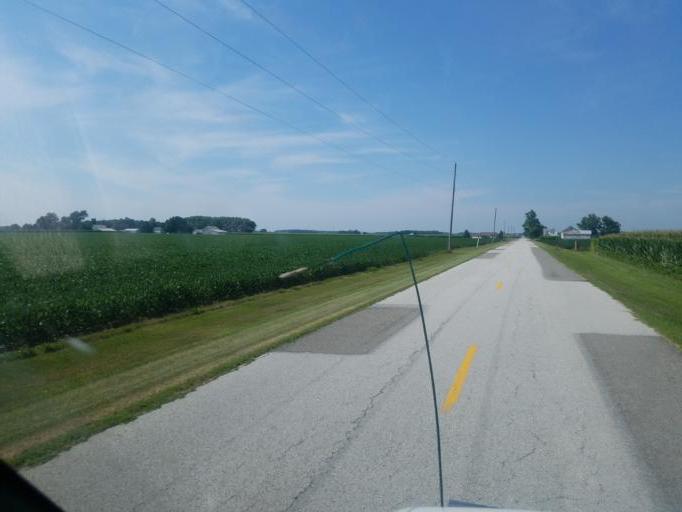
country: US
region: Ohio
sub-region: Shelby County
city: Jackson Center
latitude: 40.5296
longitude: -84.0119
